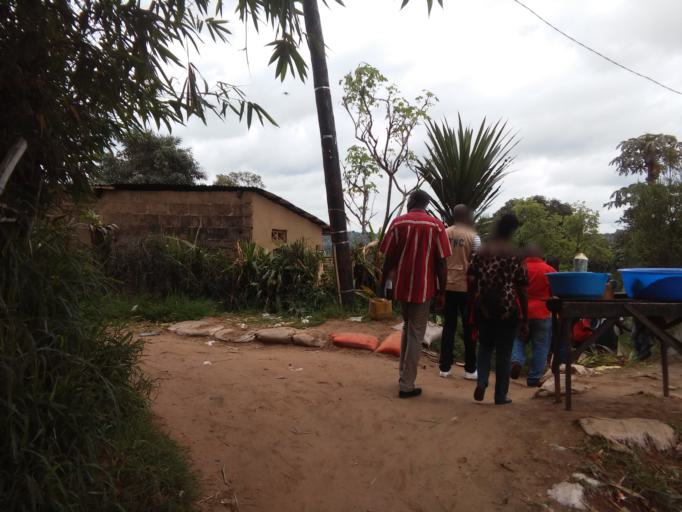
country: CD
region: Kinshasa
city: Masina
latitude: -4.4233
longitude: 15.3308
